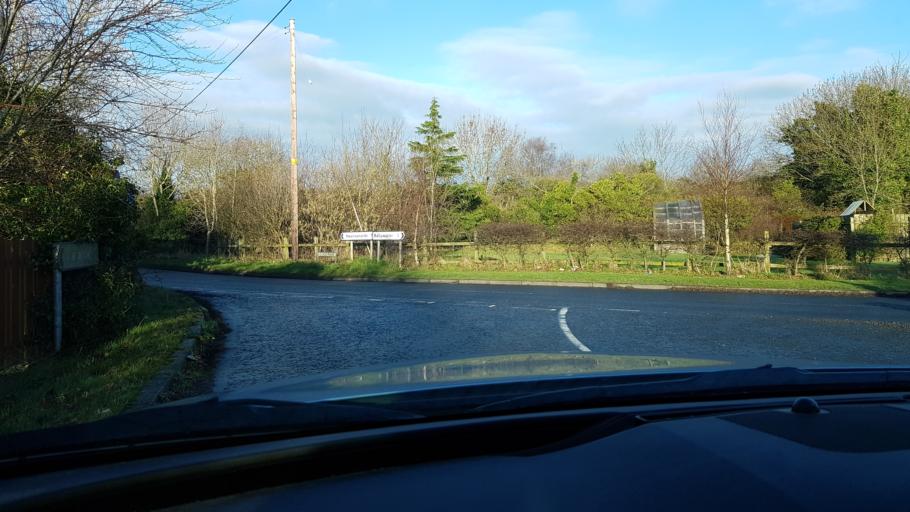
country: GB
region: Northern Ireland
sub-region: Ards District
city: Greyabbey
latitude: 54.5573
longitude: -5.5482
